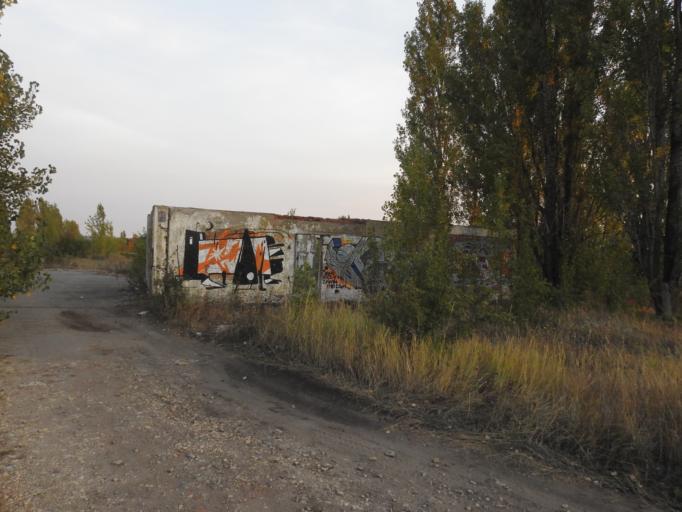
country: RU
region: Saratov
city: Sokolovyy
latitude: 51.5494
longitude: 45.8565
